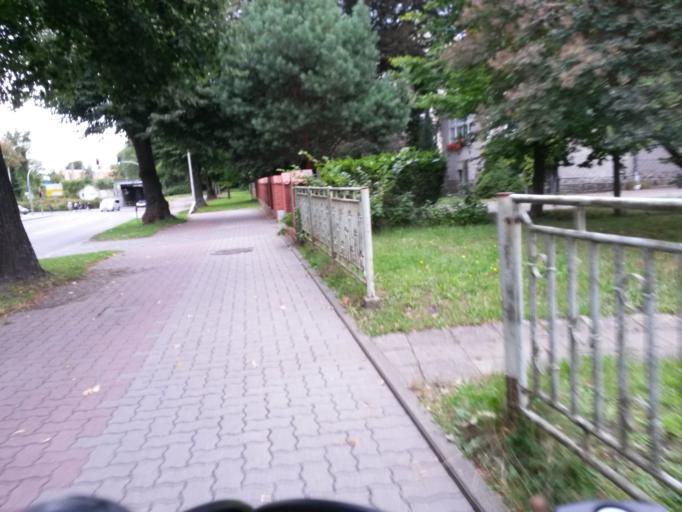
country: DE
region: Brandenburg
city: Angermunde
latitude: 53.0128
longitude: 13.9965
